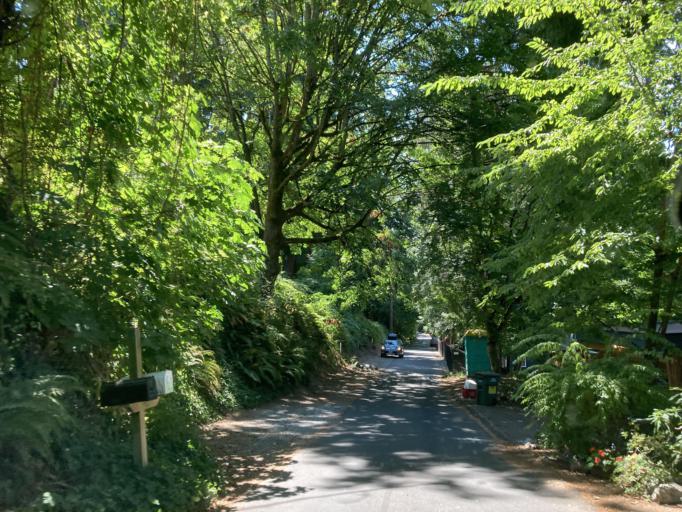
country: US
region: Washington
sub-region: Whatcom County
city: Bellingham
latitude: 48.7362
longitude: -122.4910
